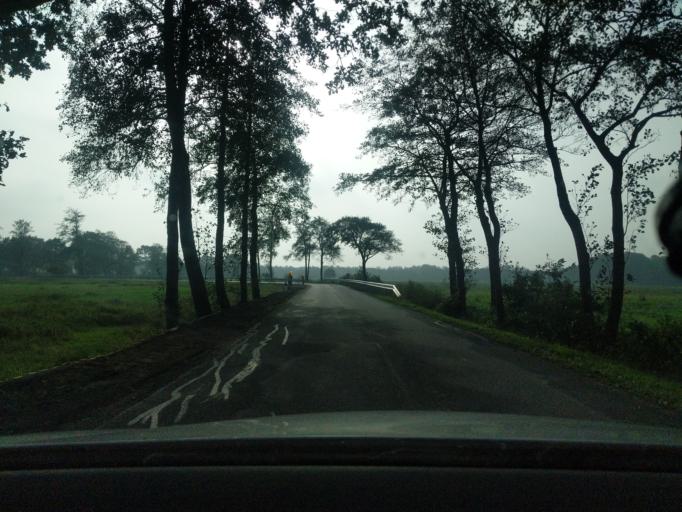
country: DE
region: Lower Saxony
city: Wanna
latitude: 53.7664
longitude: 8.7332
